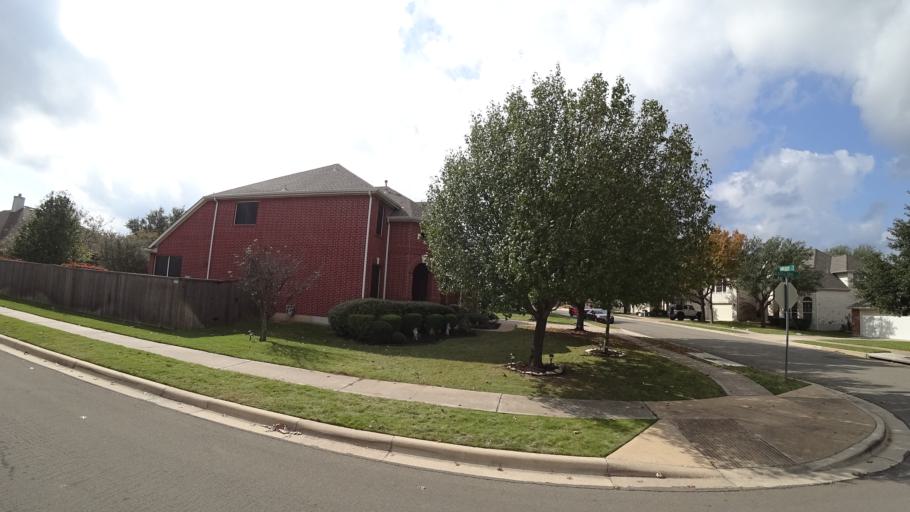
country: US
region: Texas
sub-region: Williamson County
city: Anderson Mill
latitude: 30.4254
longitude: -97.8596
